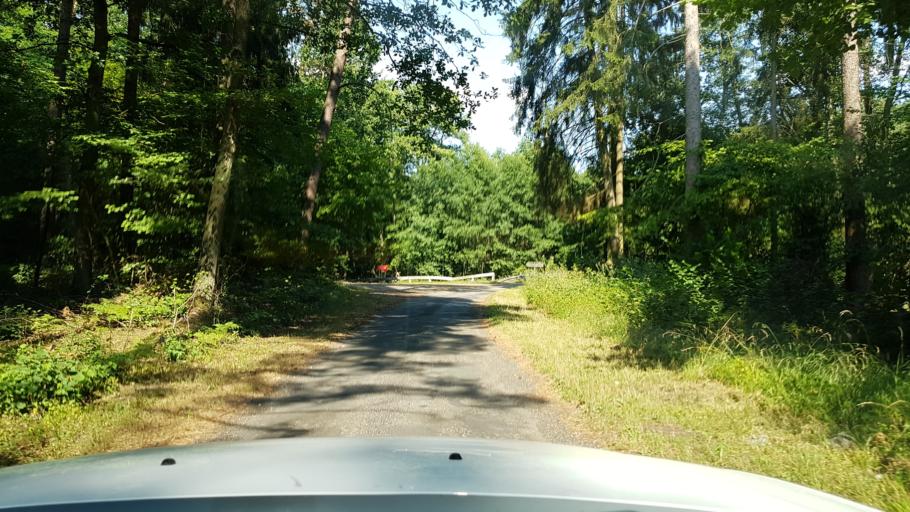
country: PL
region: West Pomeranian Voivodeship
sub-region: Powiat gryfinski
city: Moryn
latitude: 52.8110
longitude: 14.3177
